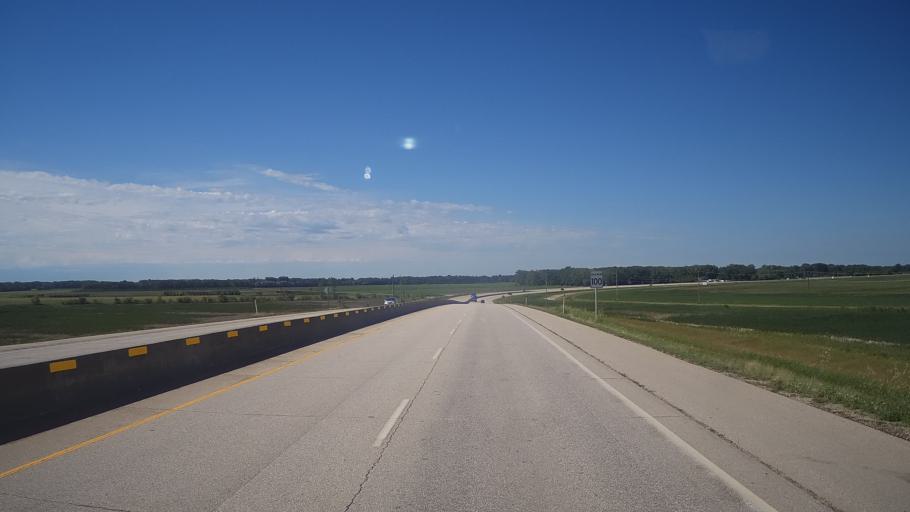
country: CA
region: Manitoba
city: Portage la Prairie
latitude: 49.9673
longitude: -98.2348
